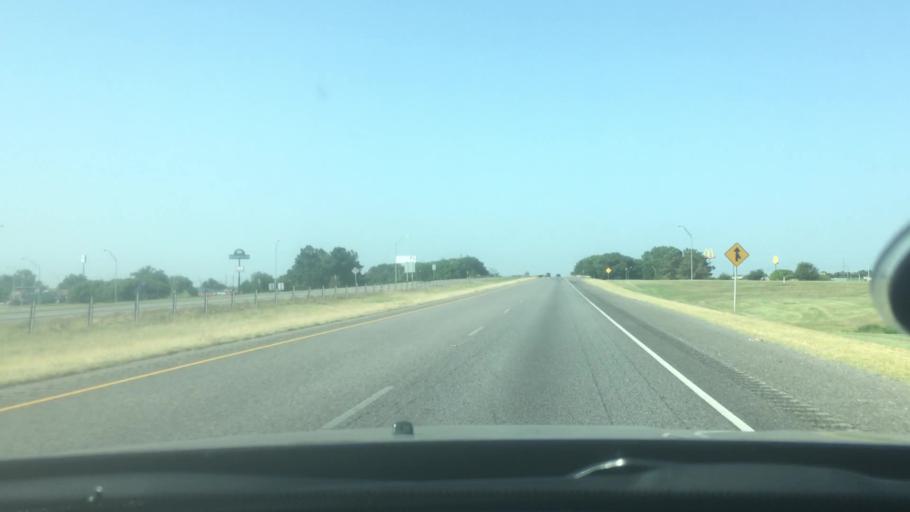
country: US
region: Oklahoma
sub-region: Bryan County
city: Durant
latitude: 34.0008
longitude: -96.4026
